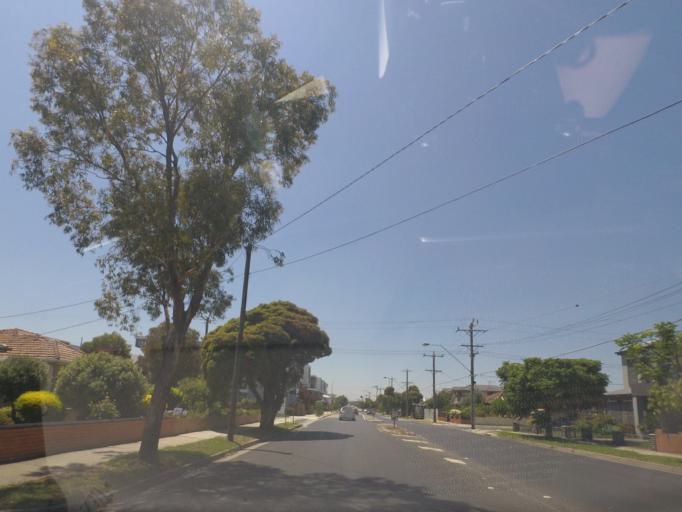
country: AU
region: Victoria
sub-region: Moreland
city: Pascoe Vale
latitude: -37.7362
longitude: 144.9375
